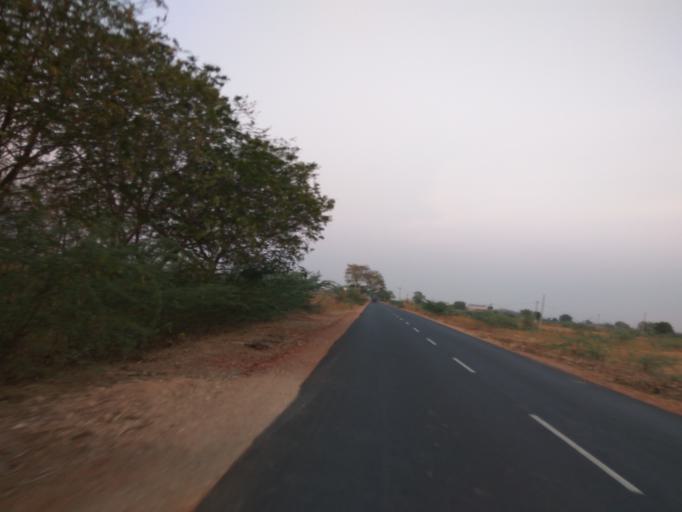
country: IN
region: Andhra Pradesh
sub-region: Prakasam
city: Markapur
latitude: 15.7515
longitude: 79.2205
